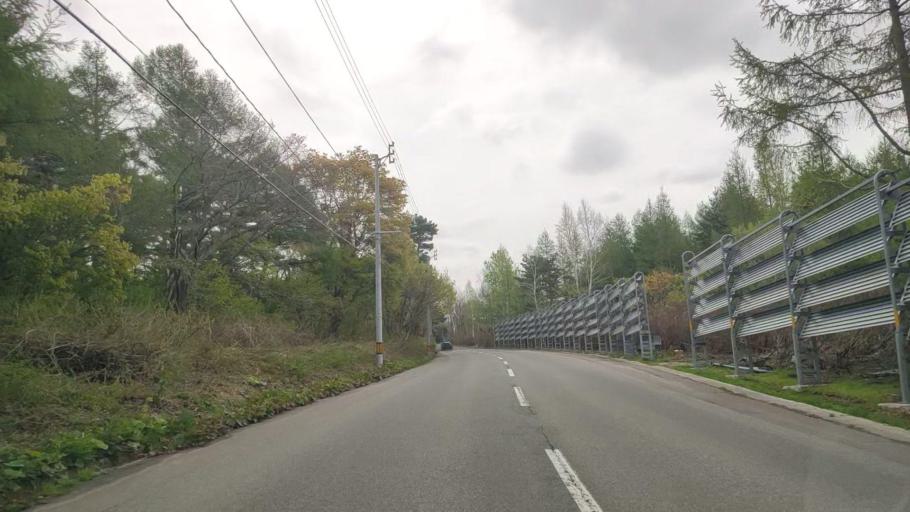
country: JP
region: Aomori
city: Aomori Shi
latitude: 40.7506
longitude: 140.8171
